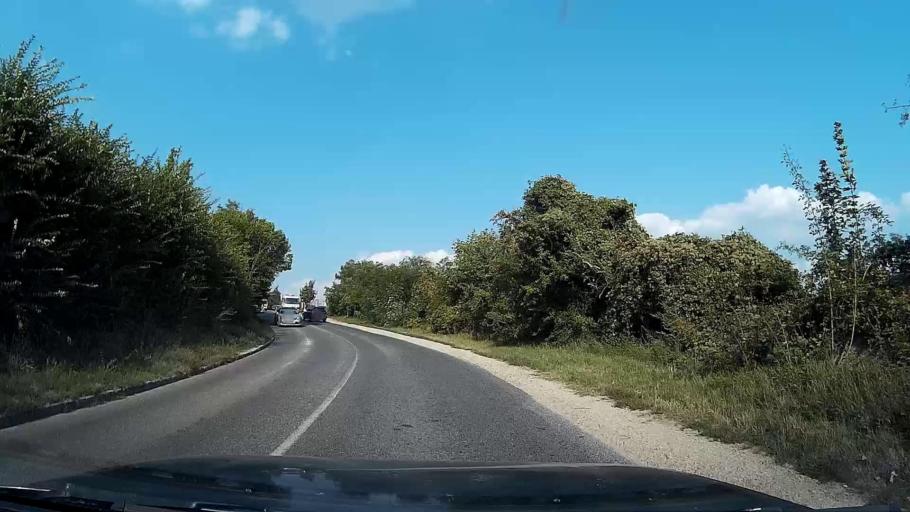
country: HU
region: Pest
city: Urom
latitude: 47.6014
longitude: 19.0201
